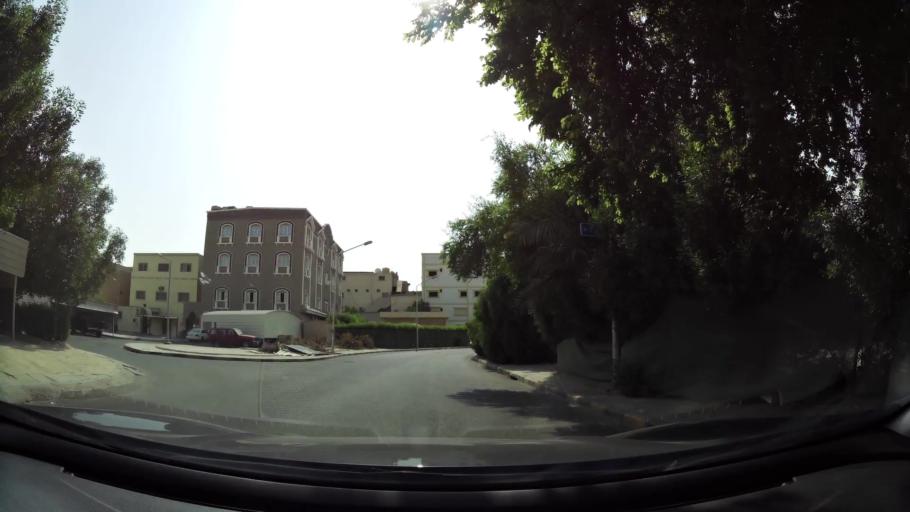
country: KW
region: Muhafazat al Jahra'
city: Al Jahra'
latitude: 29.3181
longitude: 47.6766
